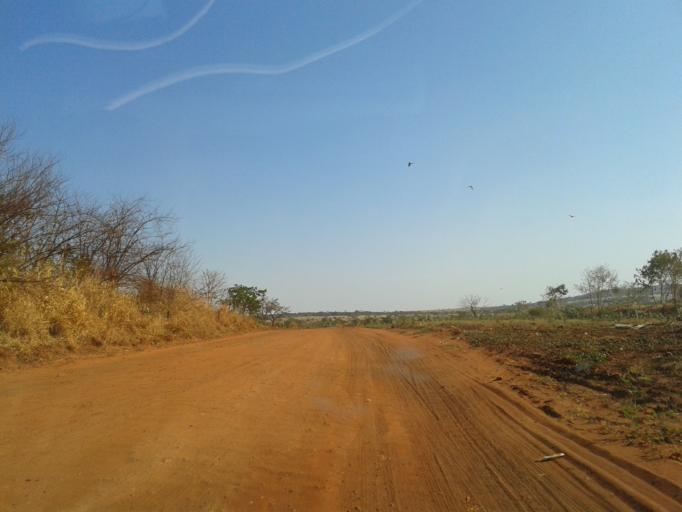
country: BR
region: Minas Gerais
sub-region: Ituiutaba
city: Ituiutaba
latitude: -18.9992
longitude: -49.4902
